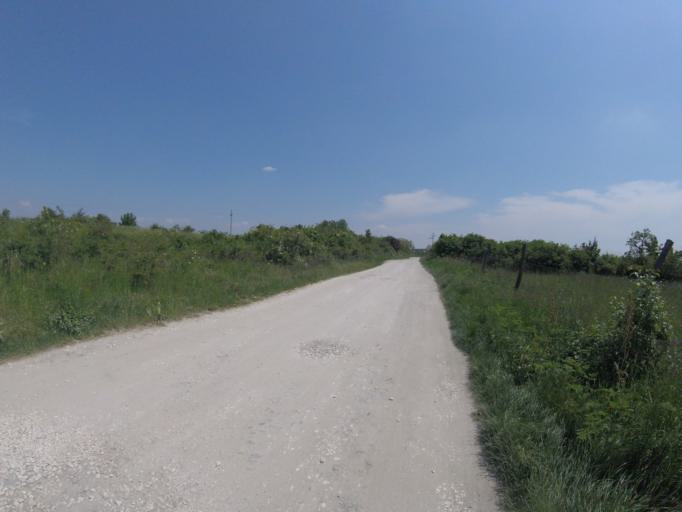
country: HU
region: Pest
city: Szentendre
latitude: 47.6772
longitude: 19.0487
